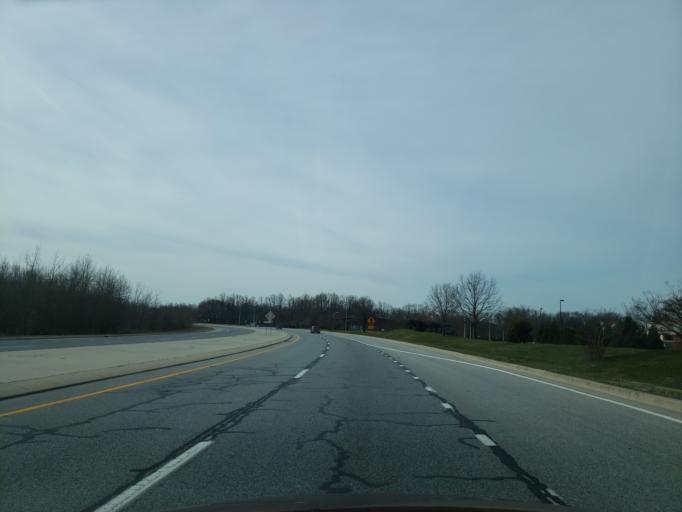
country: US
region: Delaware
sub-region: Kent County
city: Cheswold
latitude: 39.1989
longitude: -75.5571
